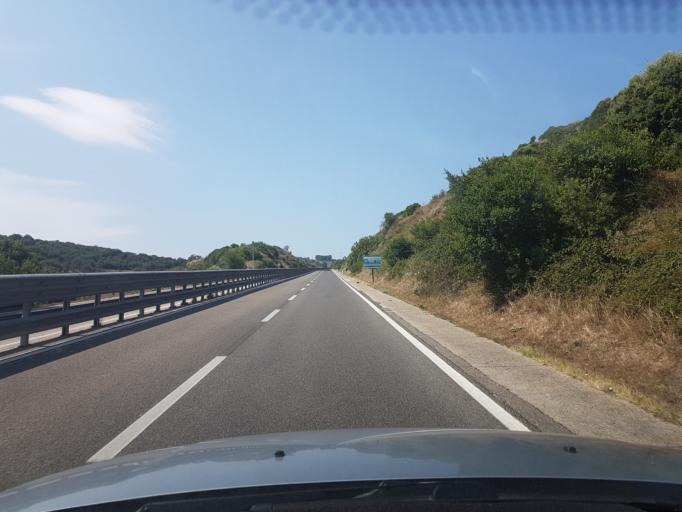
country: IT
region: Sardinia
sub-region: Provincia di Oristano
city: Soddi
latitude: 40.1383
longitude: 8.8701
